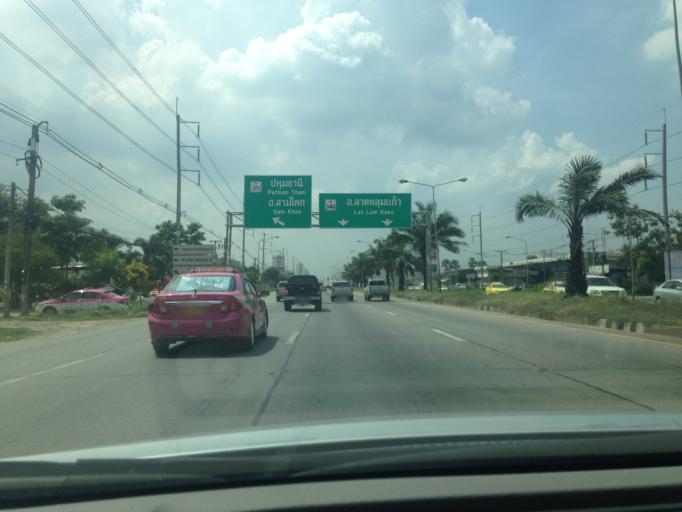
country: TH
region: Pathum Thani
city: Pathum Thani
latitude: 14.0298
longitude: 100.5323
